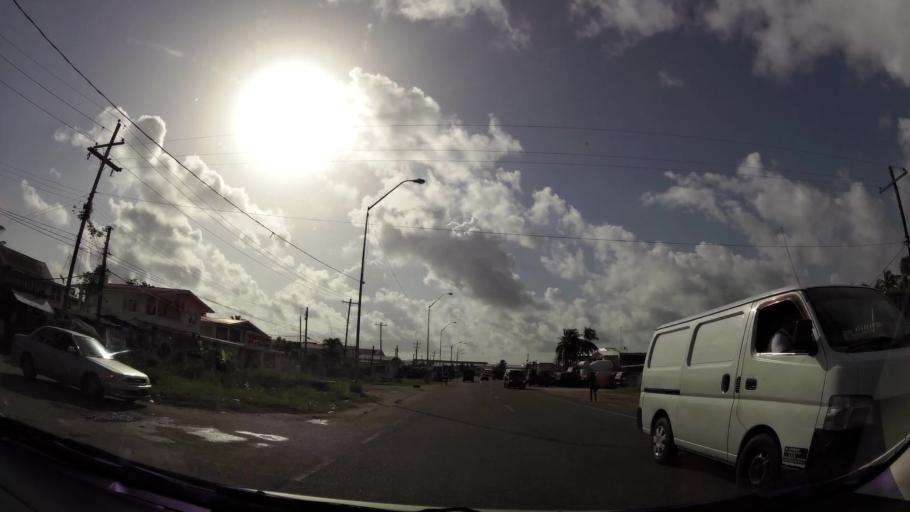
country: GY
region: Demerara-Mahaica
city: Georgetown
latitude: 6.8178
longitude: -58.0853
